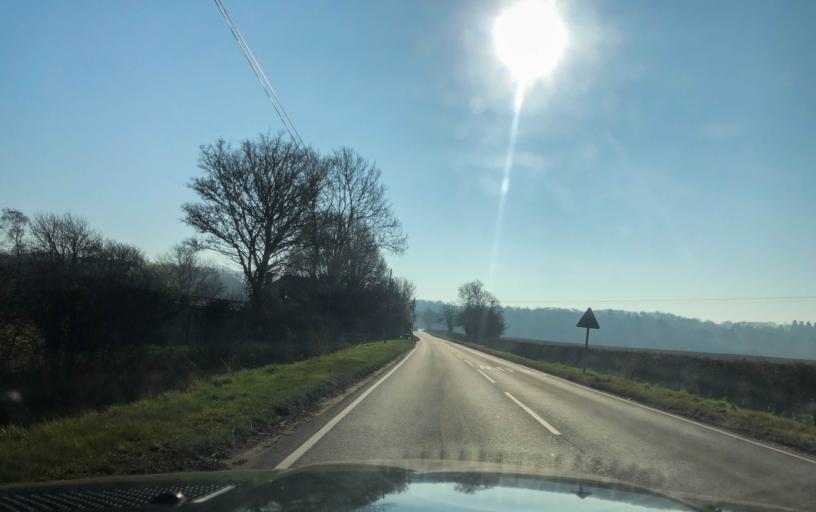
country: GB
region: England
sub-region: Warwickshire
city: Wellesbourne Mountford
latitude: 52.1852
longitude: -1.5785
